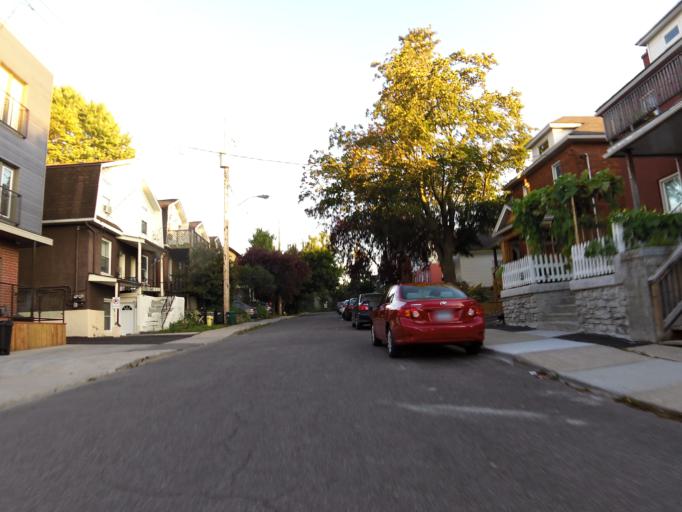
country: CA
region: Ontario
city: Ottawa
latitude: 45.4003
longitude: -75.7233
